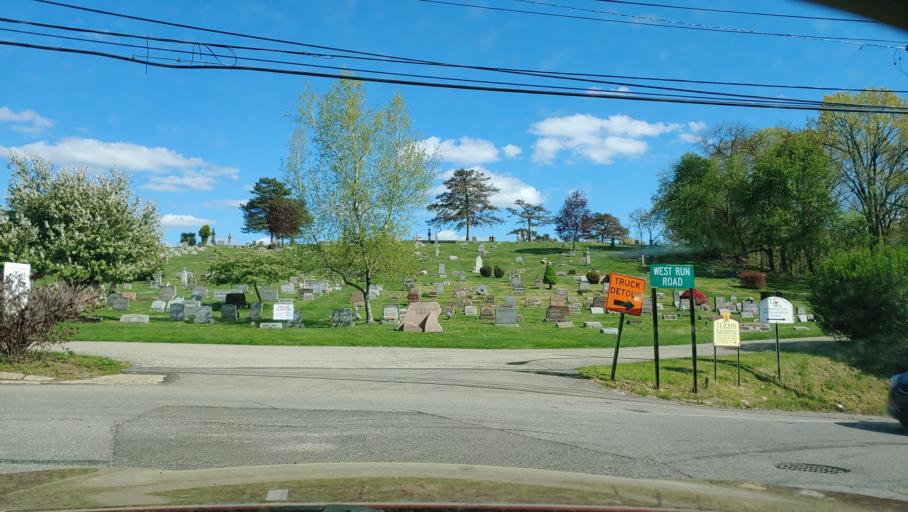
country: US
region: Pennsylvania
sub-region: Allegheny County
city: Munhall
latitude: 40.3974
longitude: -79.9028
